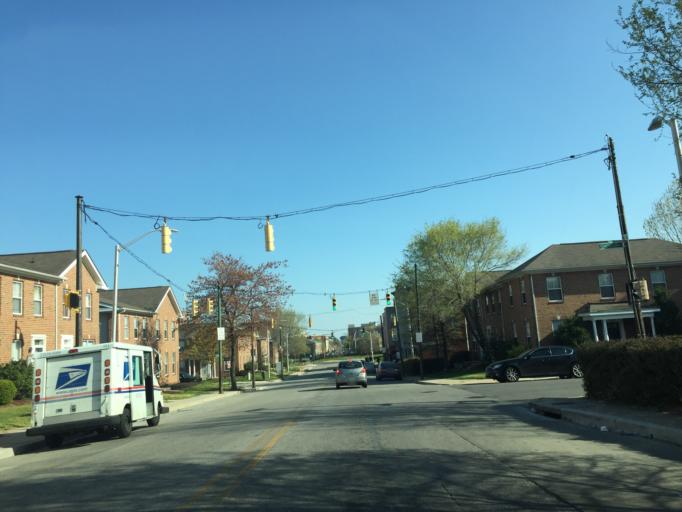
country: US
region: Maryland
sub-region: City of Baltimore
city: Baltimore
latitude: 39.2960
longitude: -76.6328
